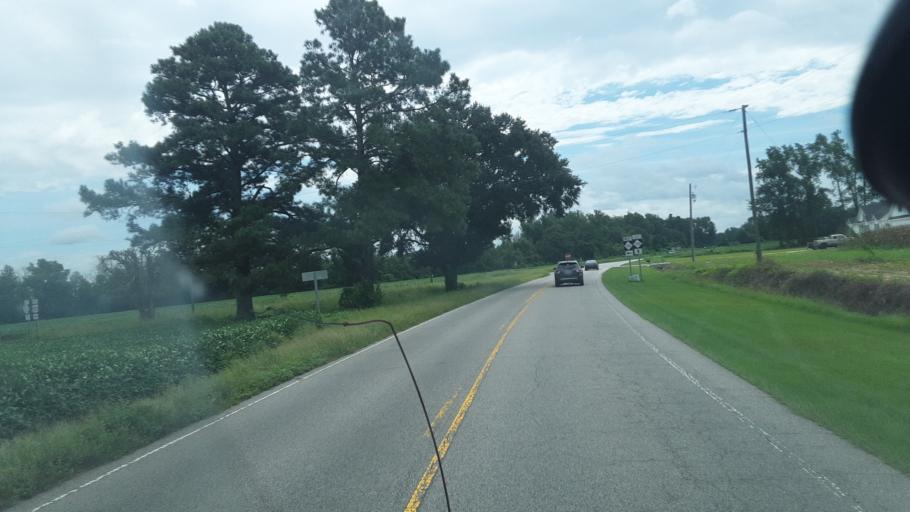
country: US
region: North Carolina
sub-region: Robeson County
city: Maxton
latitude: 34.6344
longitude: -79.3425
